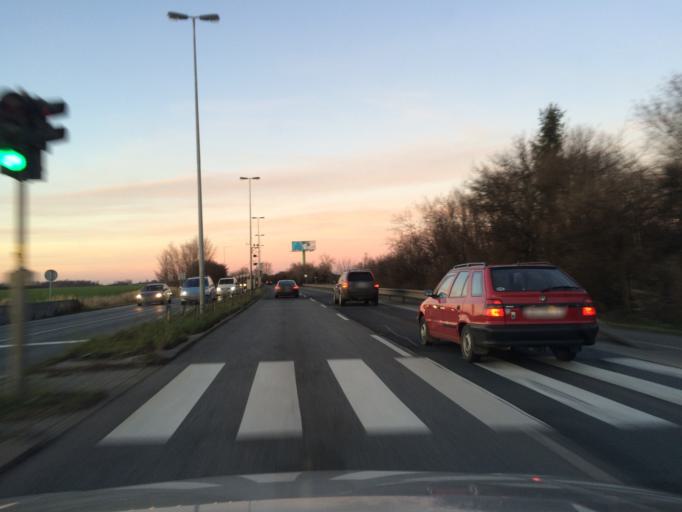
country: CZ
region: Central Bohemia
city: Tuchomerice
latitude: 50.1034
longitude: 14.2947
